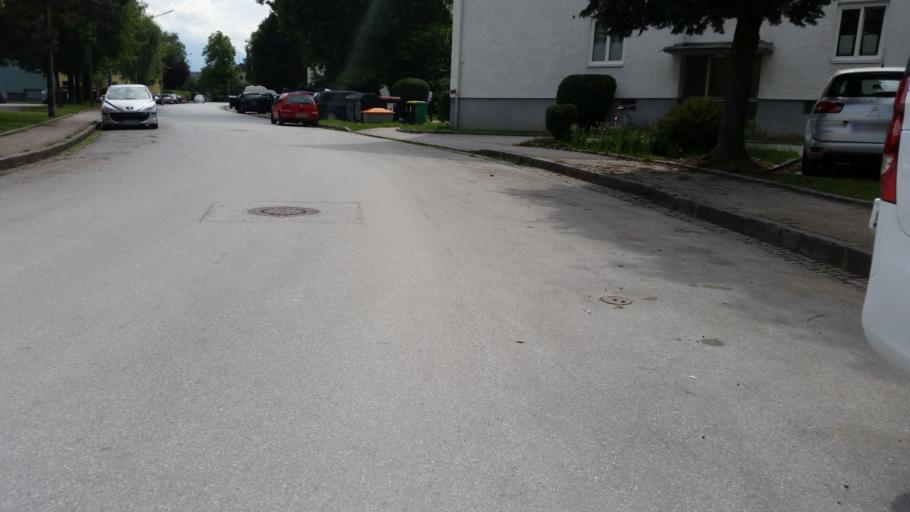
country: AT
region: Salzburg
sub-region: Politischer Bezirk Salzburg-Umgebung
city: Bergheim
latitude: 47.8144
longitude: 13.0045
